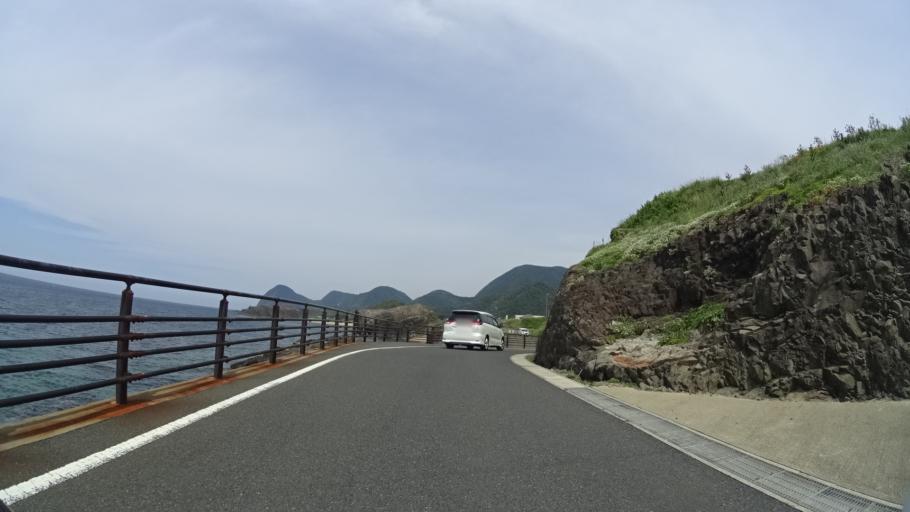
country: JP
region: Kyoto
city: Miyazu
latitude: 35.7411
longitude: 135.0983
